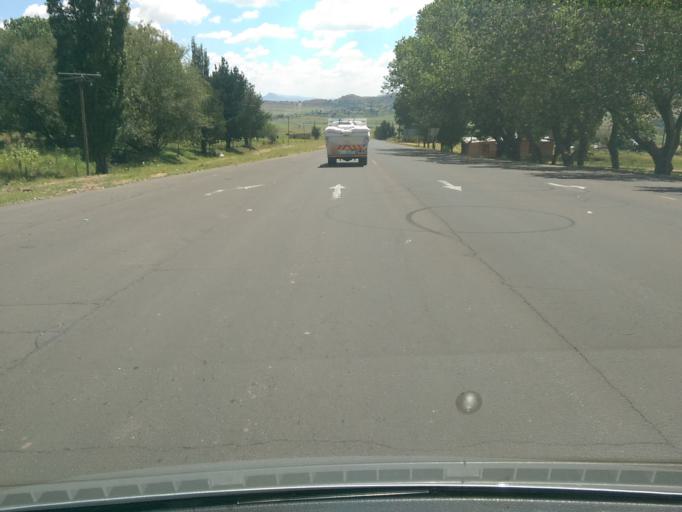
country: LS
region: Maseru
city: Nako
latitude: -29.4241
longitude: 27.6730
